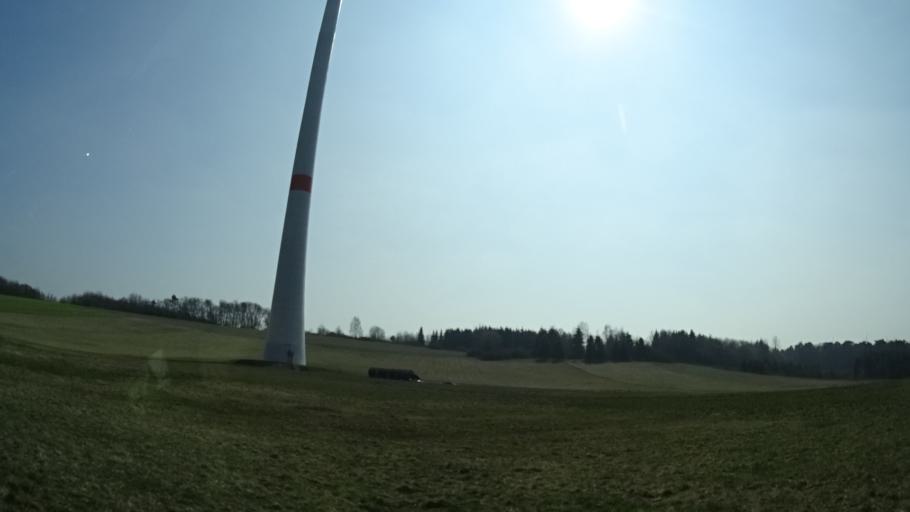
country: DE
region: Rheinland-Pfalz
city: Mettweiler
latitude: 49.5982
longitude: 7.3015
